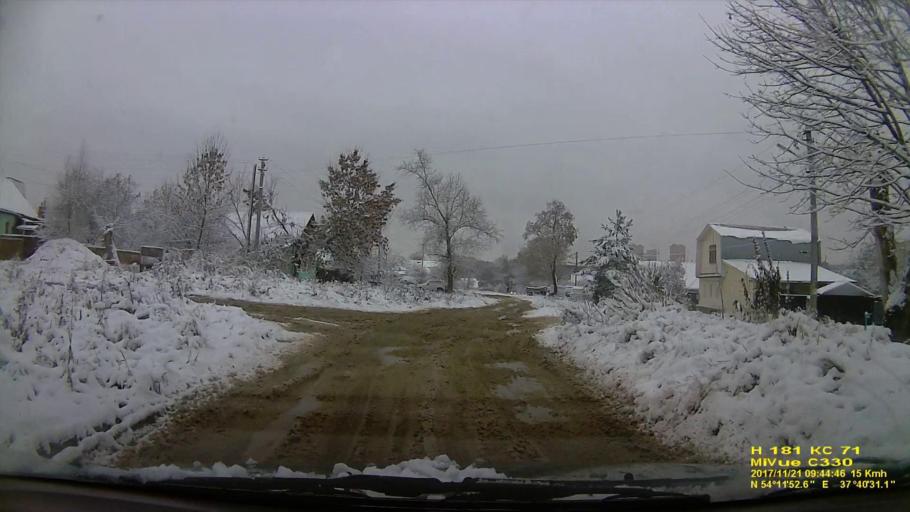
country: RU
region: Tula
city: Tula
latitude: 54.1980
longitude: 37.6752
